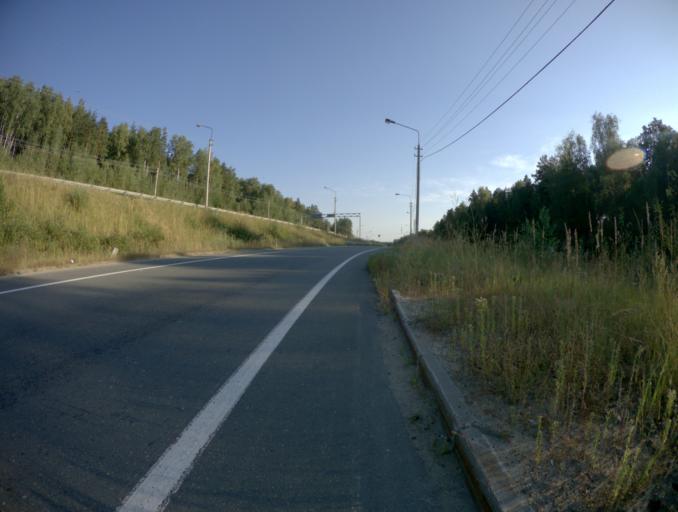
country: RU
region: Vladimir
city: Kommunar
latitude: 56.0545
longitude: 40.4388
